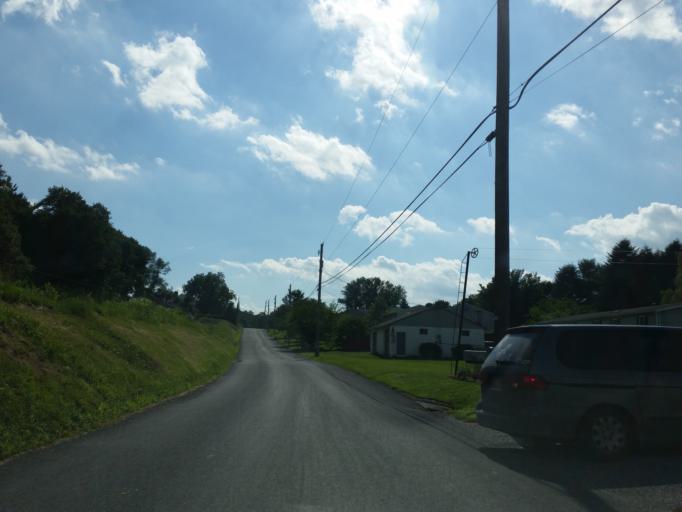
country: US
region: Pennsylvania
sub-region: Lancaster County
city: Strasburg
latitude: 39.9672
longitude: -76.1773
